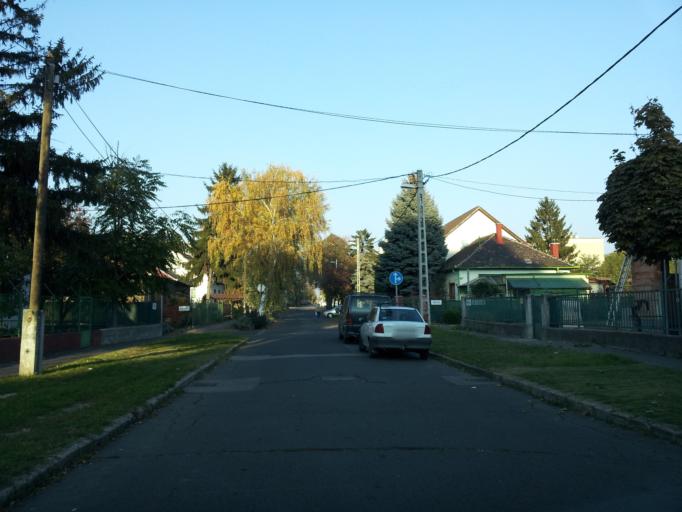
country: HU
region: Budapest
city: Budapest X. keruelet
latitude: 47.4763
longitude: 19.1610
